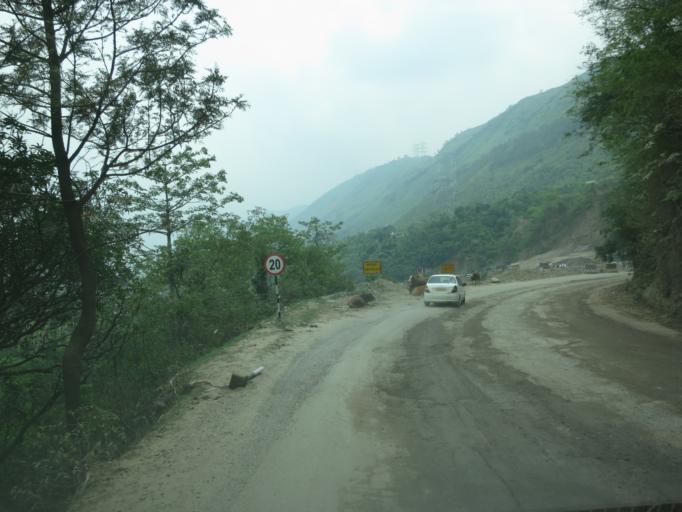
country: IN
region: Himachal Pradesh
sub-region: Mandi
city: Sundarnagar
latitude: 31.4541
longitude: 76.8586
